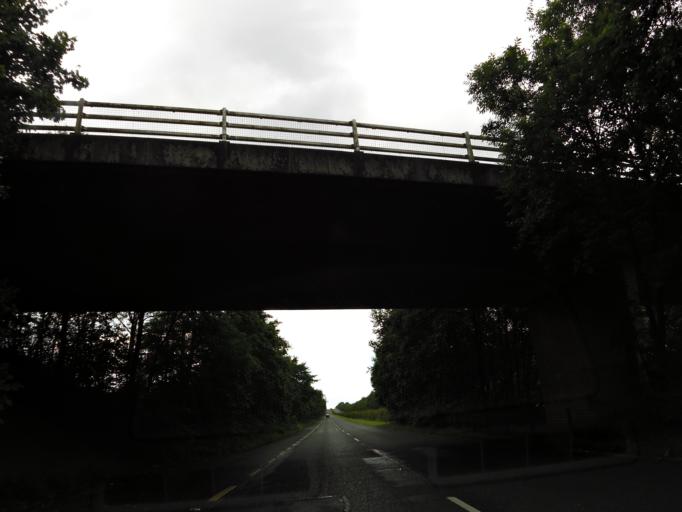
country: IE
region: Connaught
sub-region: County Galway
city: Oranmore
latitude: 53.2783
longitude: -8.9451
